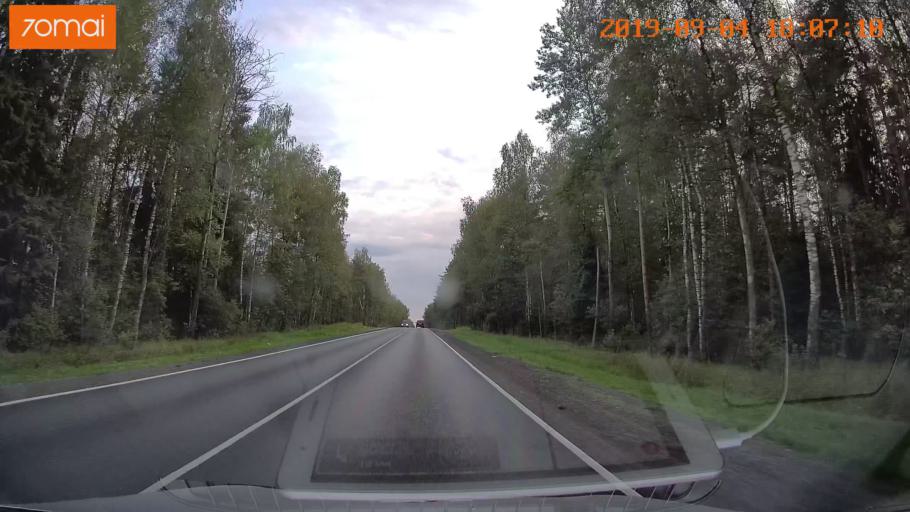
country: RU
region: Moskovskaya
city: Khorlovo
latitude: 55.4225
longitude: 38.8049
